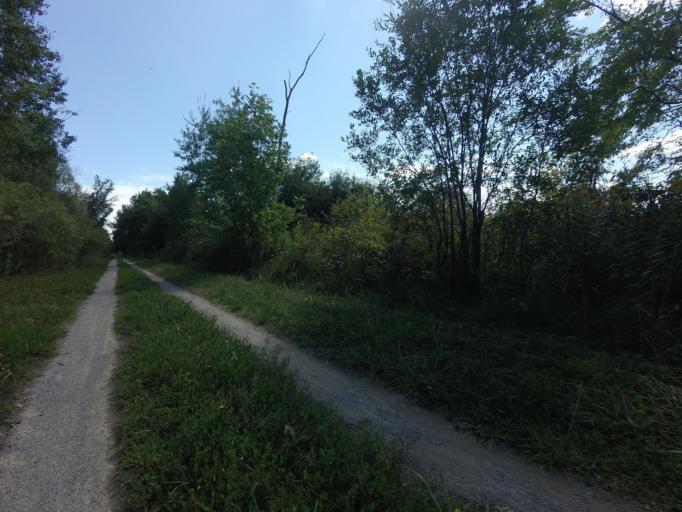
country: CA
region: Ontario
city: Orangeville
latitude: 43.7750
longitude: -80.1972
